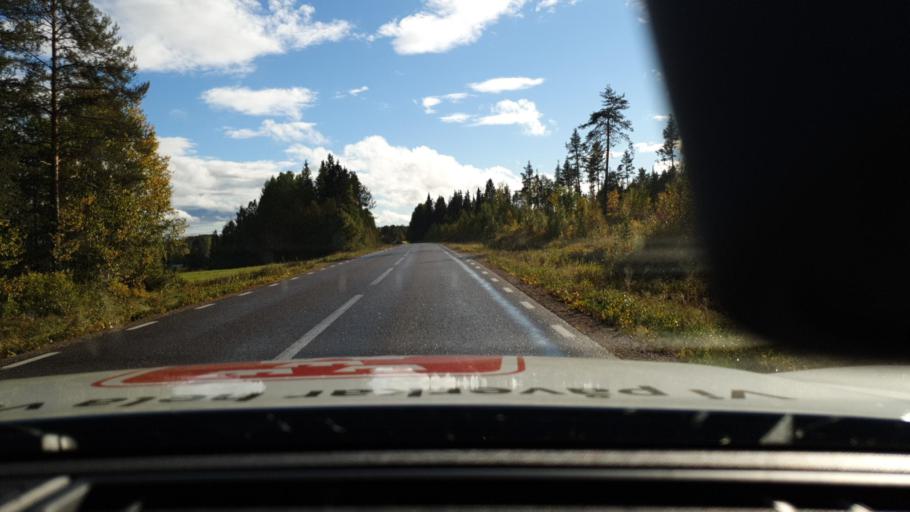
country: SE
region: Norrbotten
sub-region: Overkalix Kommun
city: OEverkalix
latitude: 66.7684
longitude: 22.6878
